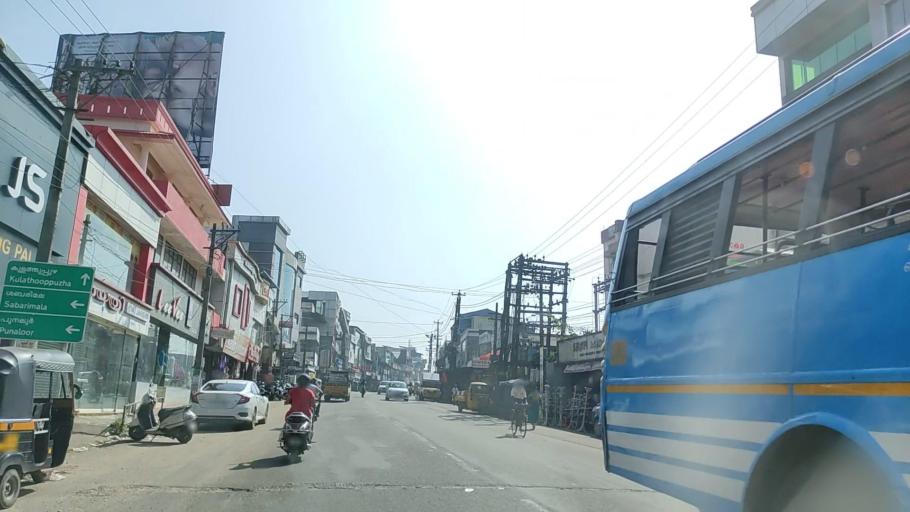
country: IN
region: Kerala
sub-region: Kollam
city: Punalur
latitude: 8.9283
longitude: 76.9114
